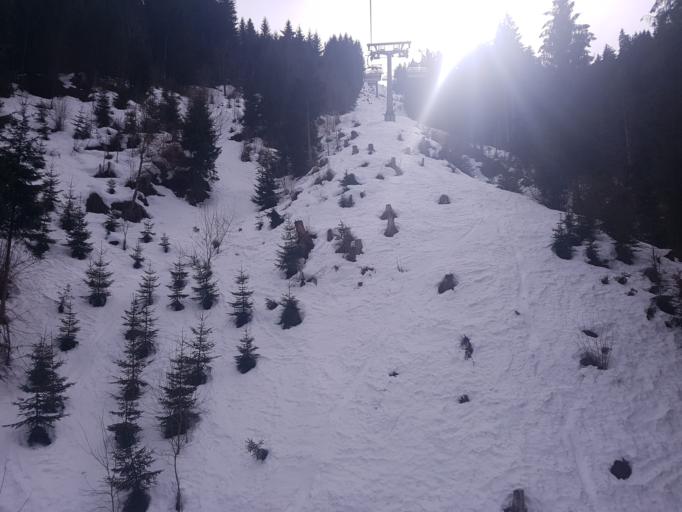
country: AT
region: Tyrol
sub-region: Politischer Bezirk Kufstein
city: Worgl
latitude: 47.4418
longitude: 12.0859
